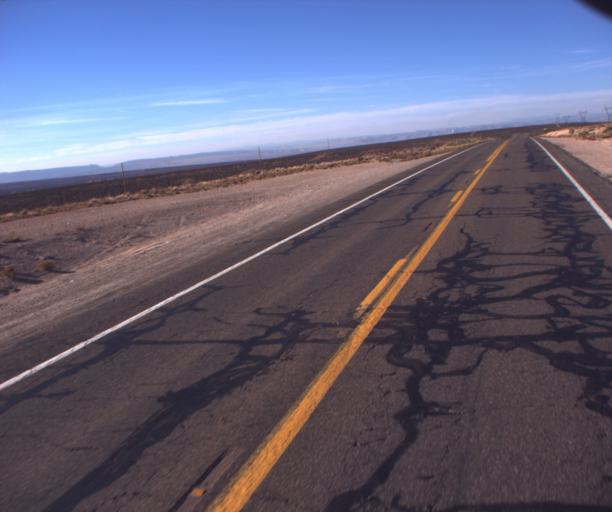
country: US
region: Arizona
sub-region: Coconino County
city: LeChee
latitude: 36.7978
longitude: -111.3009
